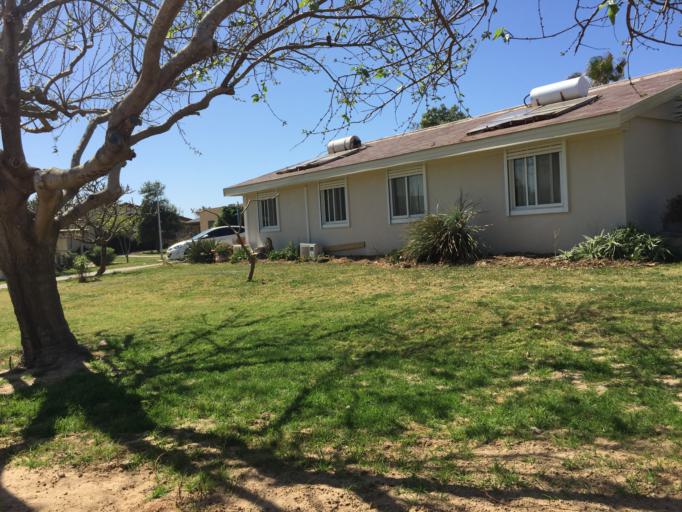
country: IL
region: Haifa
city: Qesarya
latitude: 32.4904
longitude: 34.8901
